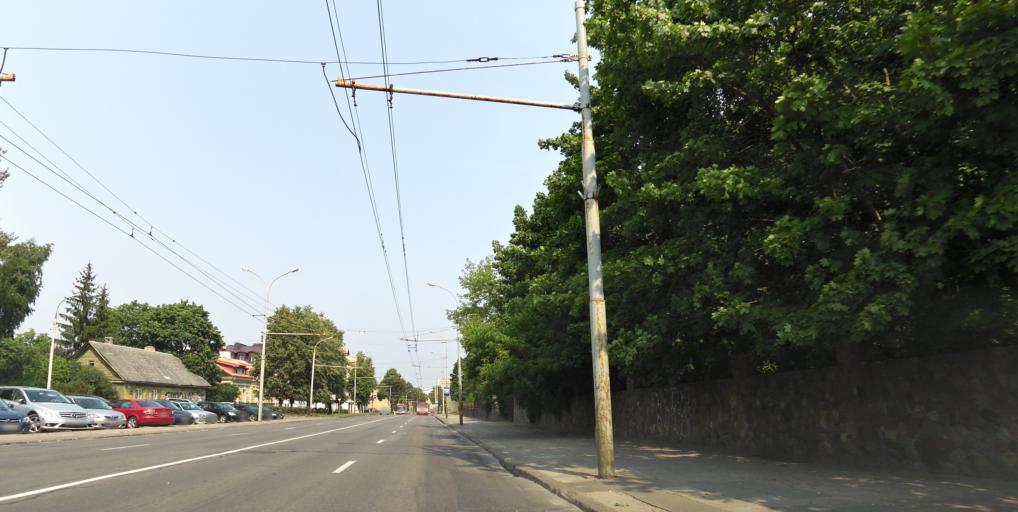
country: LT
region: Vilnius County
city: Rasos
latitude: 54.6985
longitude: 25.3088
